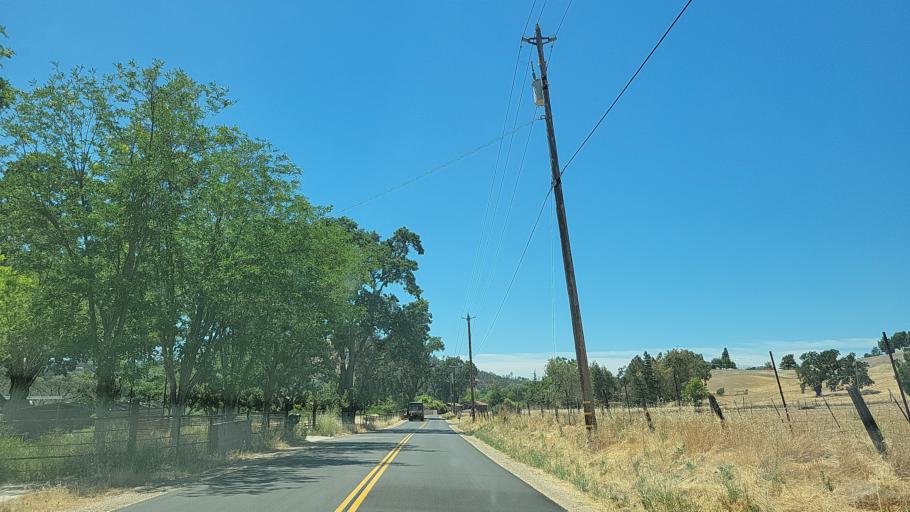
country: US
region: California
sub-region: San Luis Obispo County
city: Atascadero
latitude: 35.4872
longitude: -120.6353
